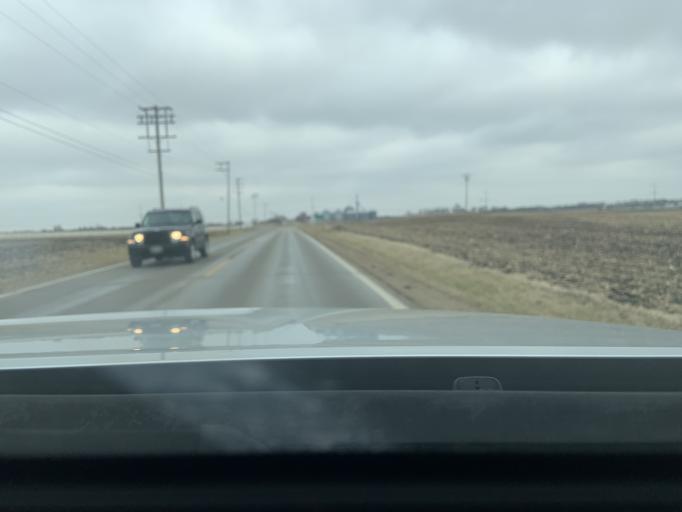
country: US
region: Illinois
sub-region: LaSalle County
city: Seneca
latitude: 41.3682
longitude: -88.6129
